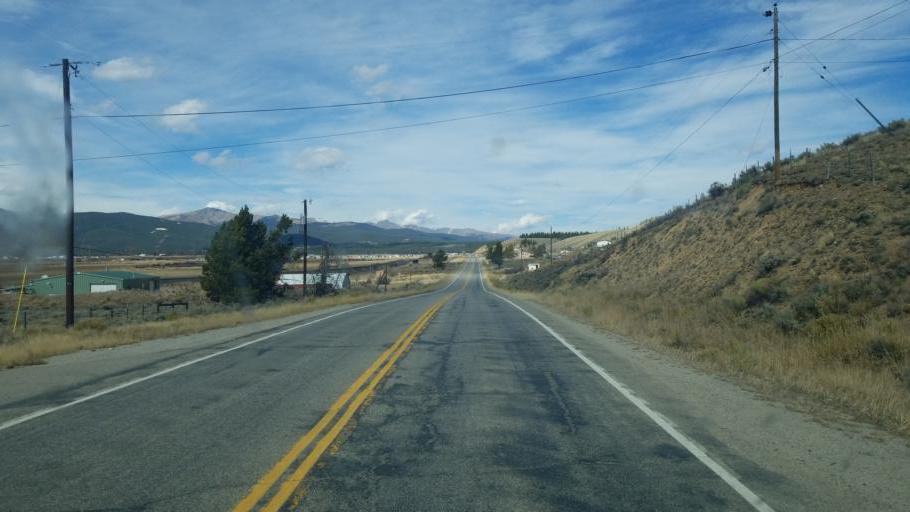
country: US
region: Colorado
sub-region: Lake County
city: Leadville North
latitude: 39.2067
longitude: -106.3449
